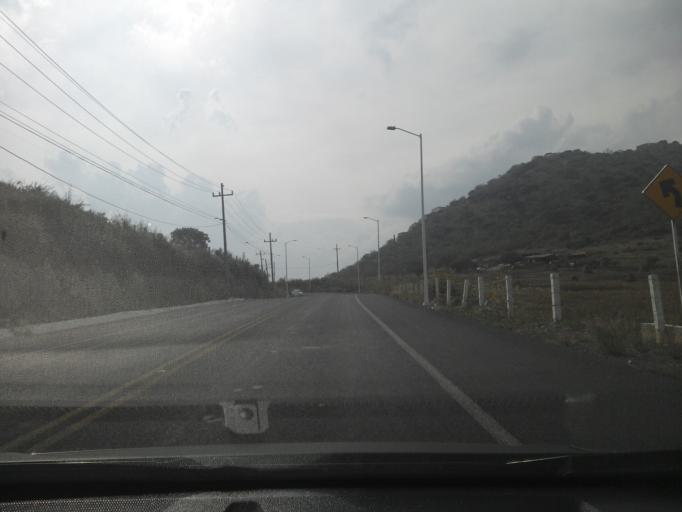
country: MX
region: Jalisco
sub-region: Tlajomulco de Zuniga
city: Lomas del Sur
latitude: 20.4872
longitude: -103.4255
